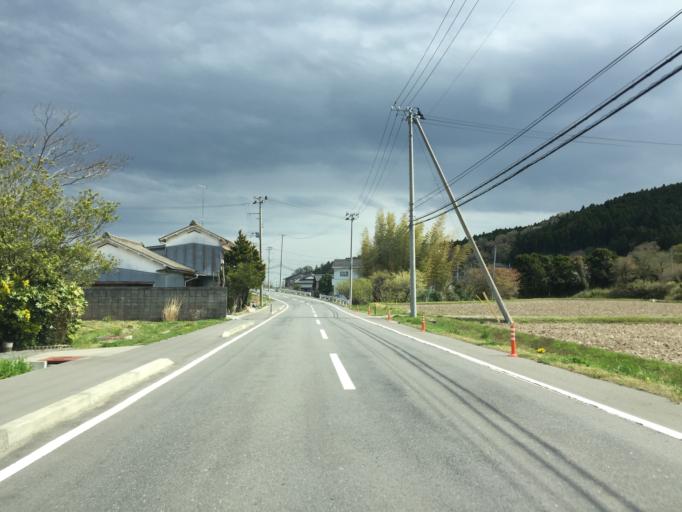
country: JP
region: Fukushima
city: Iwaki
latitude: 37.1568
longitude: 140.9777
